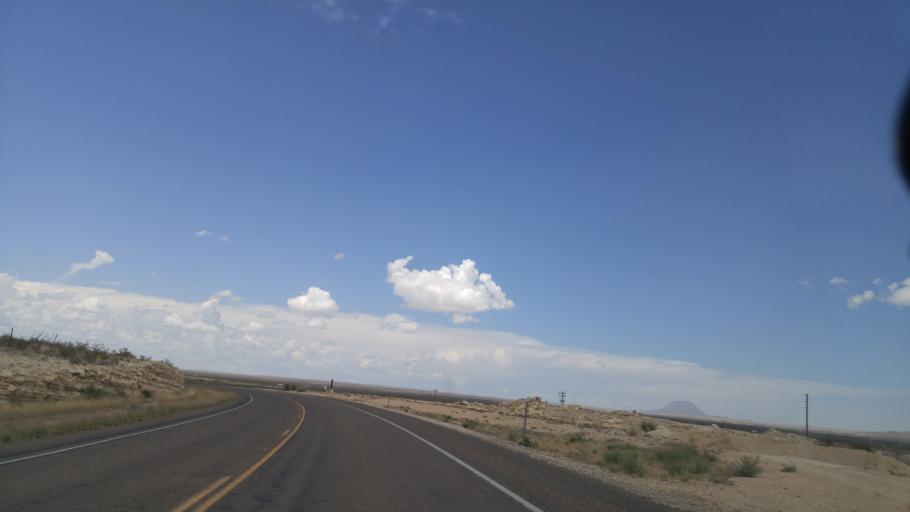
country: US
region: Texas
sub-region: Brewster County
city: Alpine
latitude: 29.5981
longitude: -103.5600
